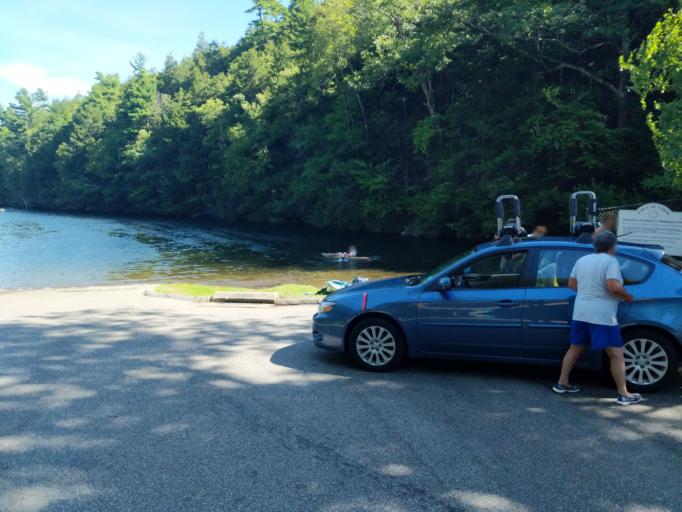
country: US
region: Massachusetts
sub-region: Hampden County
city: Holland
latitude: 42.0048
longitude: -72.1289
